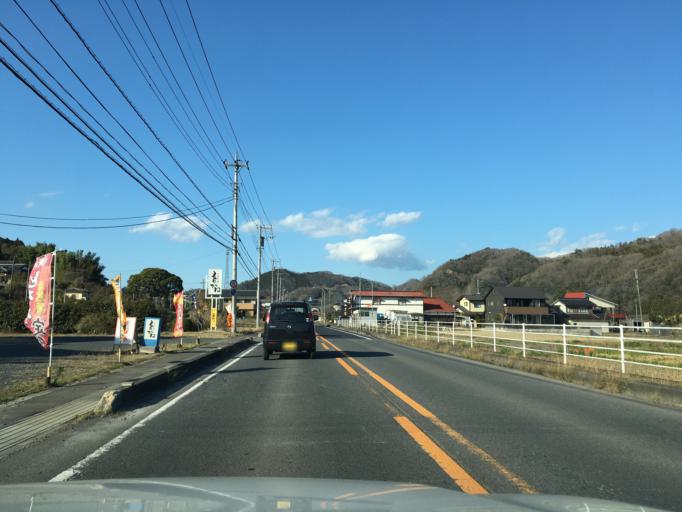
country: JP
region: Ibaraki
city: Omiya
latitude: 36.6420
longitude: 140.3917
